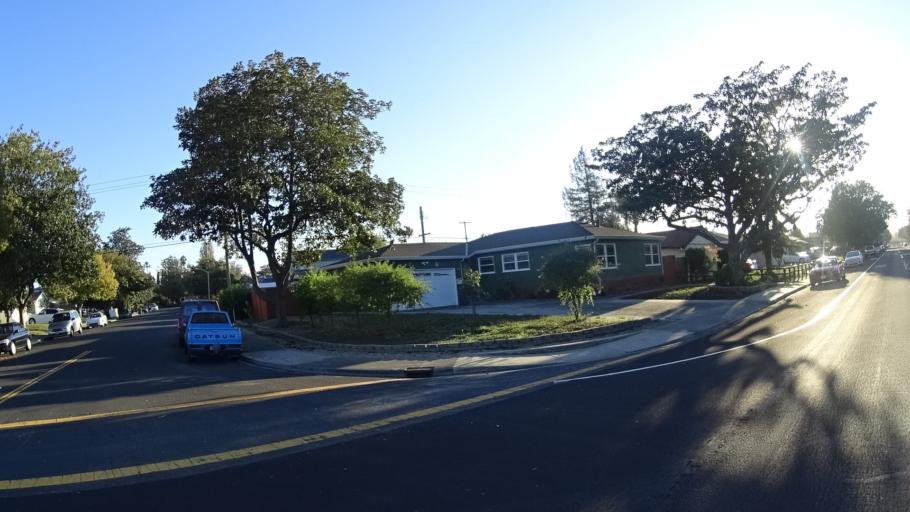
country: US
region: California
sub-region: Santa Clara County
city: Santa Clara
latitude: 37.3668
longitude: -121.9774
